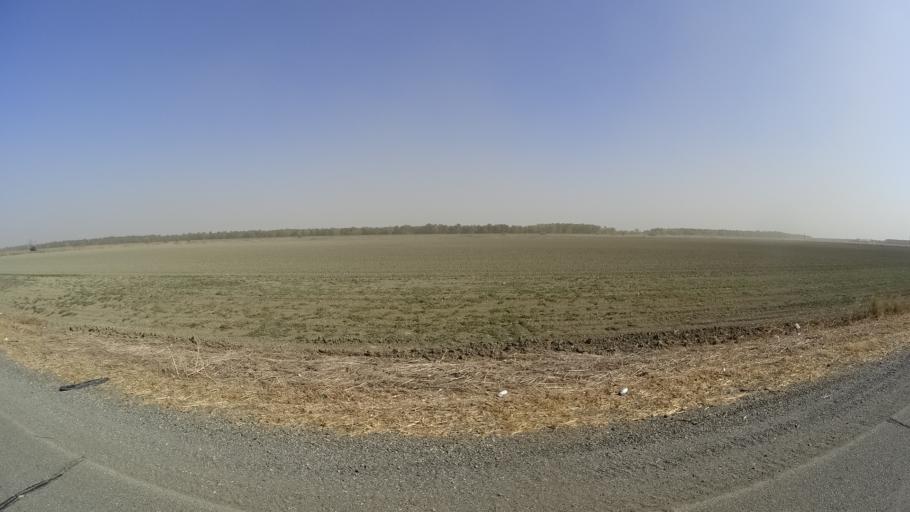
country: US
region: California
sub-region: Yolo County
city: Woodland
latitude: 38.6956
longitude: -121.7282
